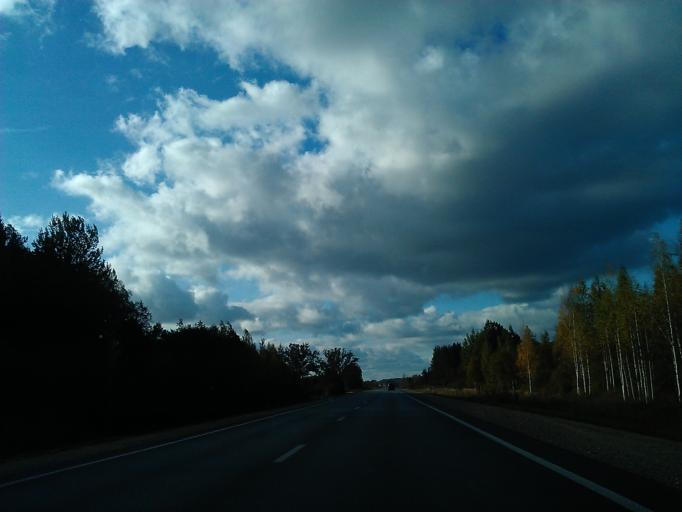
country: LV
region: Skriveri
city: Skriveri
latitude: 56.7245
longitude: 25.1830
